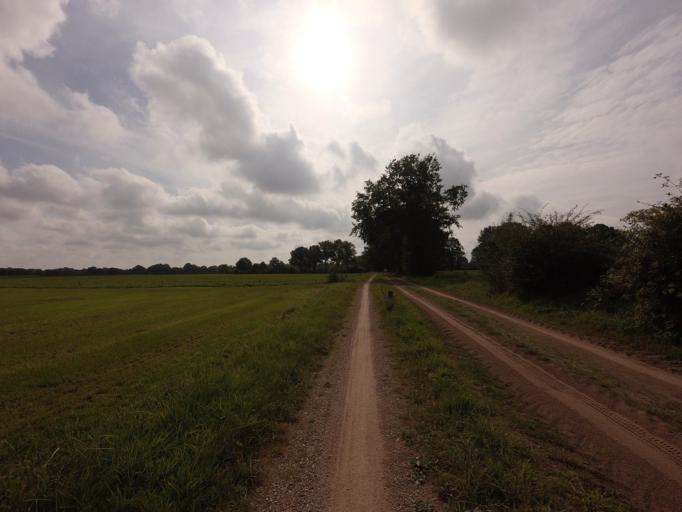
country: DE
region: Lower Saxony
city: Lage
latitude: 52.4254
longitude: 6.9517
